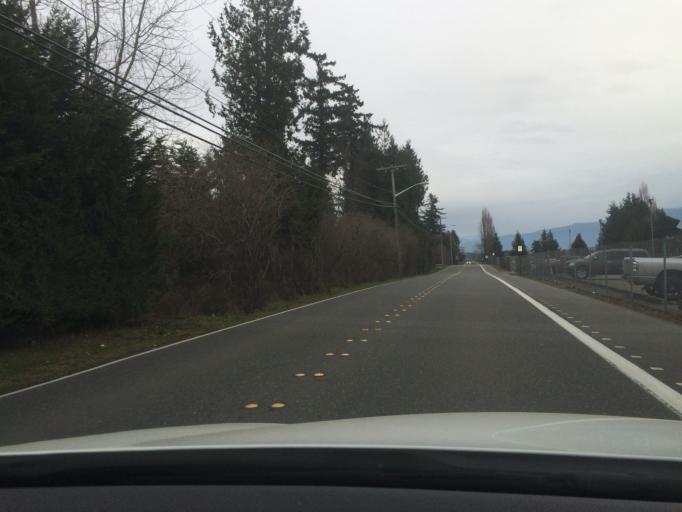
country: US
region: Washington
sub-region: Whatcom County
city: Lynden
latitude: 48.9532
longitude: -122.4270
